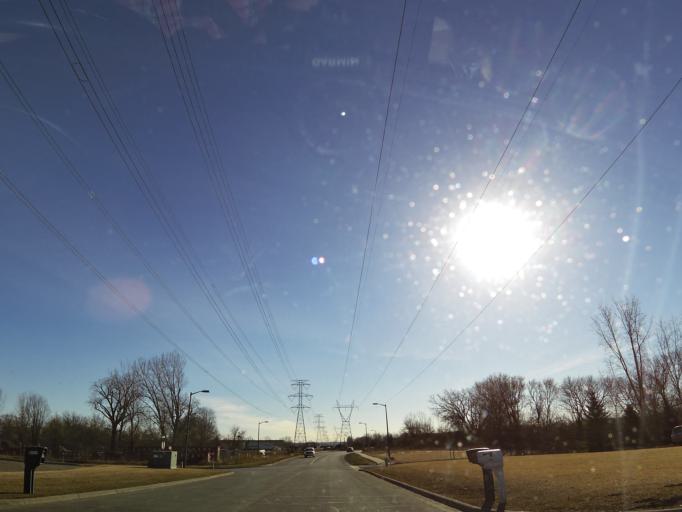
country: US
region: Minnesota
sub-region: Scott County
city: Savage
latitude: 44.7759
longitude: -93.3881
